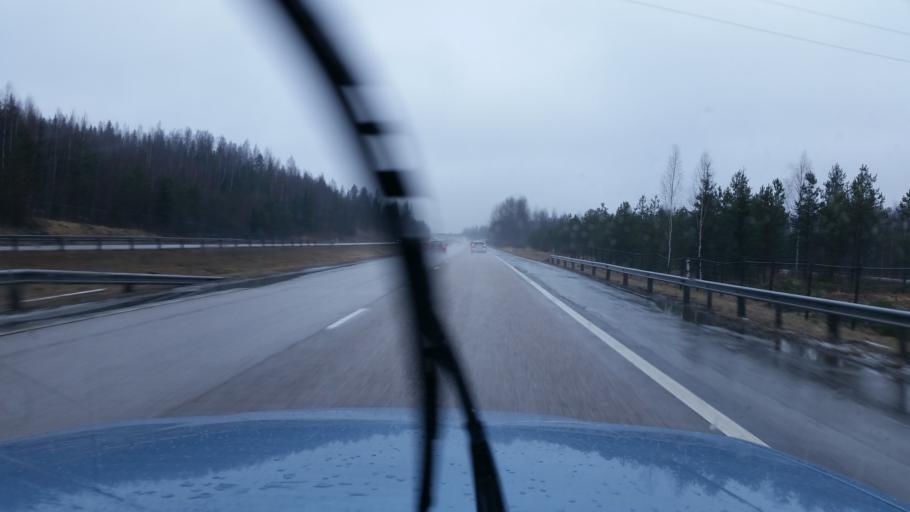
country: FI
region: Uusimaa
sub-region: Helsinki
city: Hyvinge
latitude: 60.6520
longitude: 24.8021
